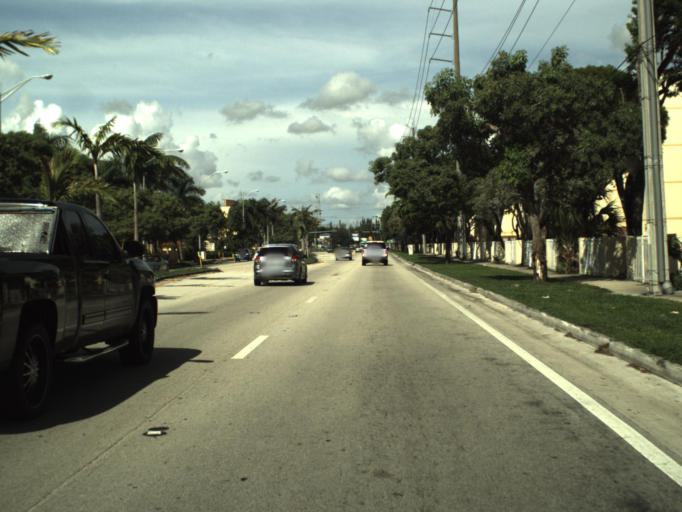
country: US
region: Florida
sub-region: Miami-Dade County
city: Country Club
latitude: 25.9416
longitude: -80.3162
